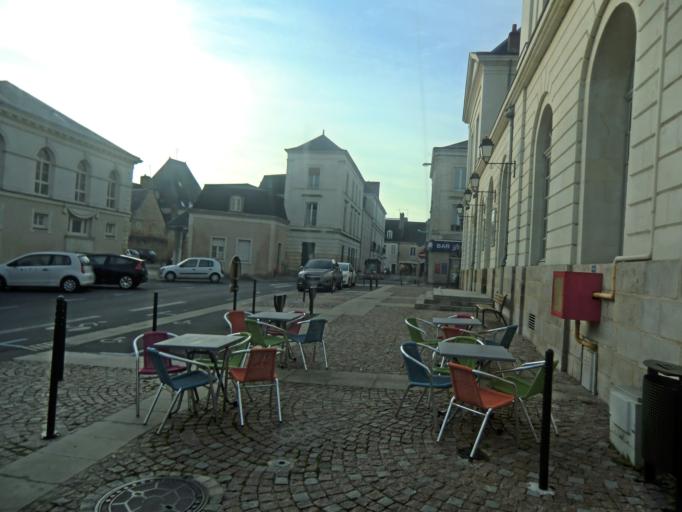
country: FR
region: Pays de la Loire
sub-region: Departement de la Sarthe
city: La Fleche
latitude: 47.7005
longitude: -0.0726
